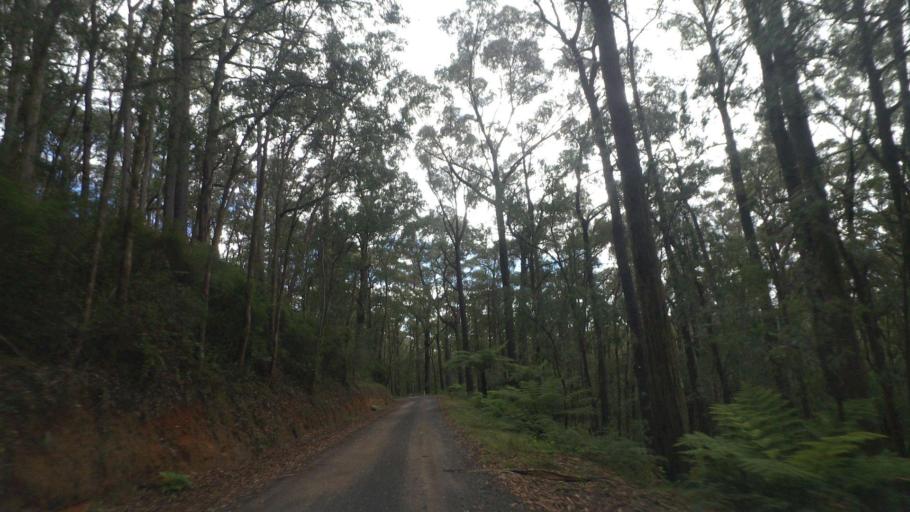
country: AU
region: Victoria
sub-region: Cardinia
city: Gembrook
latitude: -37.8941
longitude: 145.6559
